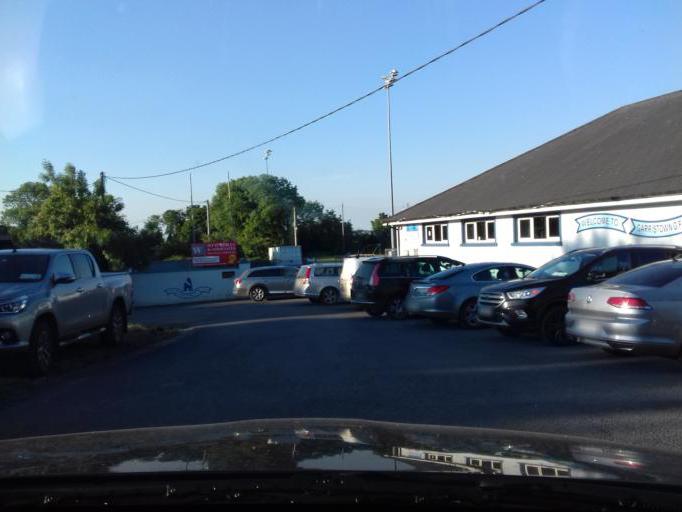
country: IE
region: Leinster
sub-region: An Mhi
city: Ashbourne
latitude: 53.5659
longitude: -6.3784
